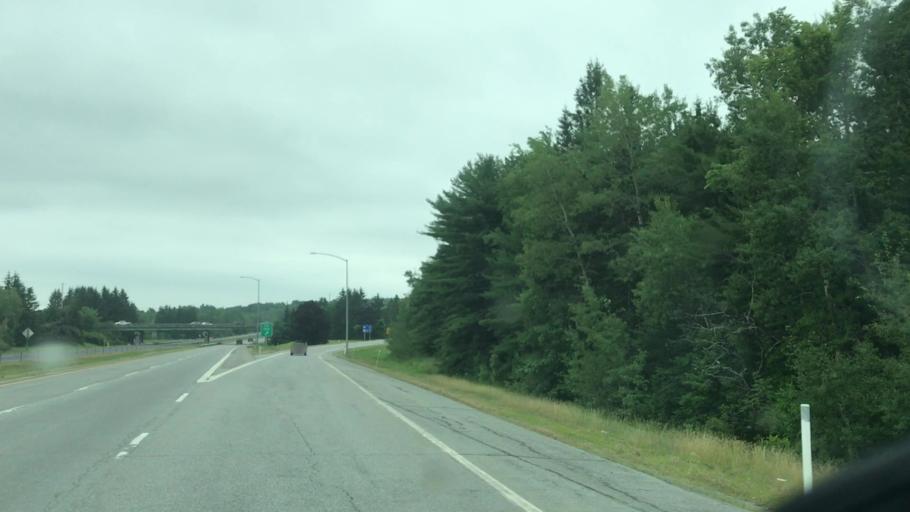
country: US
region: Maine
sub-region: Penobscot County
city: Orono
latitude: 44.9054
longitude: -68.6934
